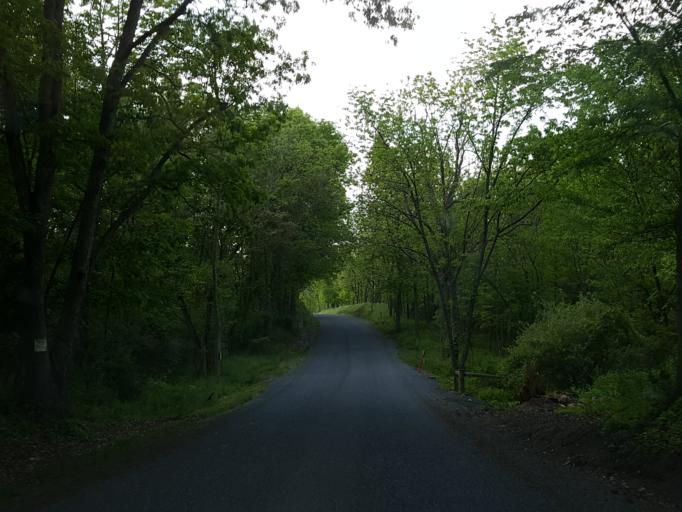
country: US
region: Pennsylvania
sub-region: Lebanon County
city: Campbelltown
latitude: 40.2134
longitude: -76.5709
